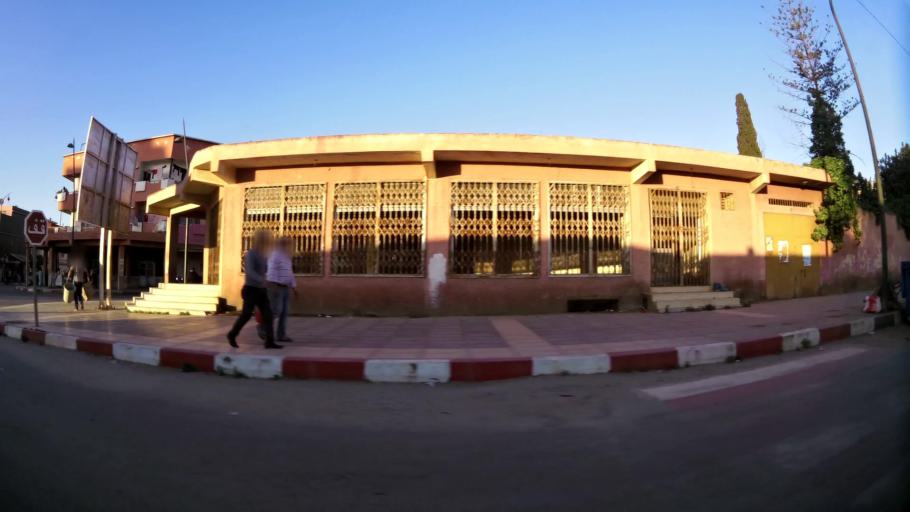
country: MA
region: Oriental
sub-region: Berkane-Taourirt
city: Berkane
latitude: 34.9208
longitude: -2.3301
